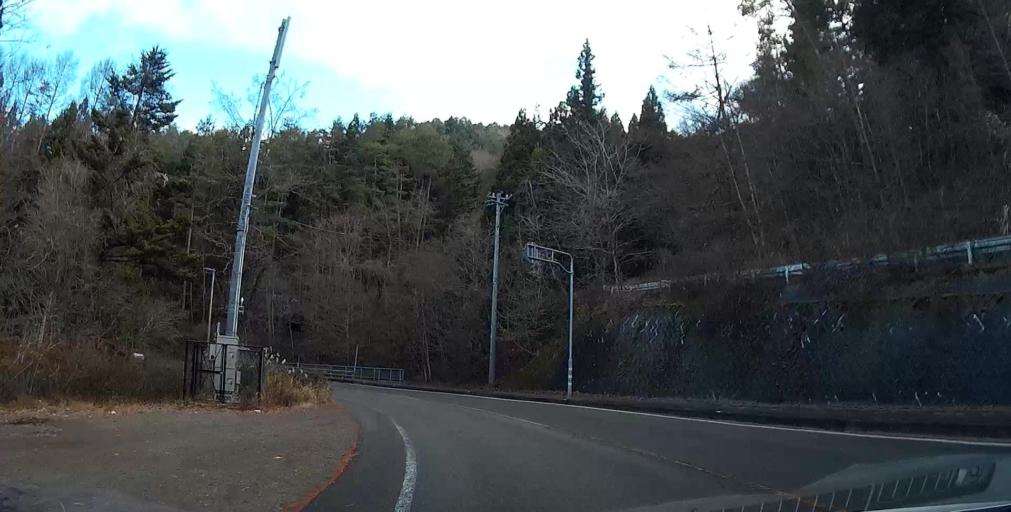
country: JP
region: Yamanashi
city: Fujikawaguchiko
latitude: 35.4787
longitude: 138.8288
